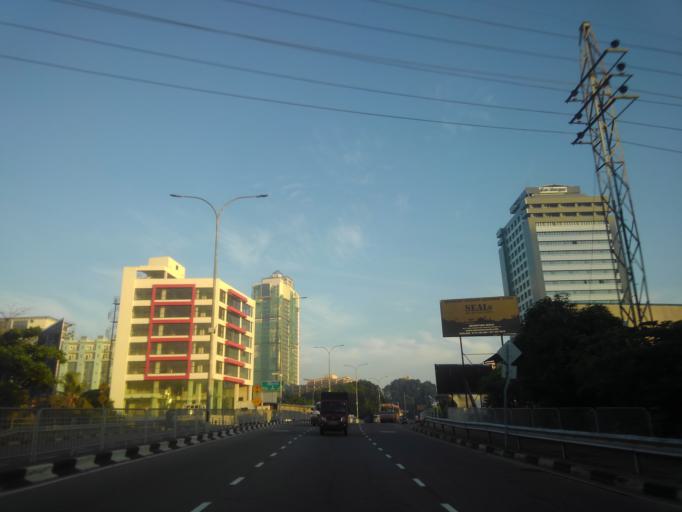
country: LK
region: Western
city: Pita Kotte
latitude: 6.8876
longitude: 79.8771
